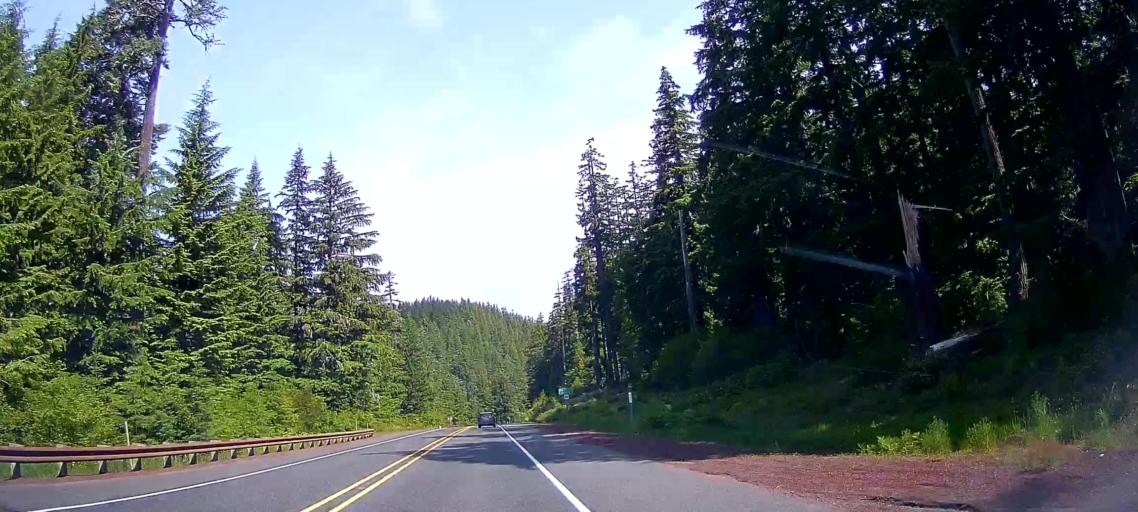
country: US
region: Oregon
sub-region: Clackamas County
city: Mount Hood Village
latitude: 45.2067
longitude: -121.6972
